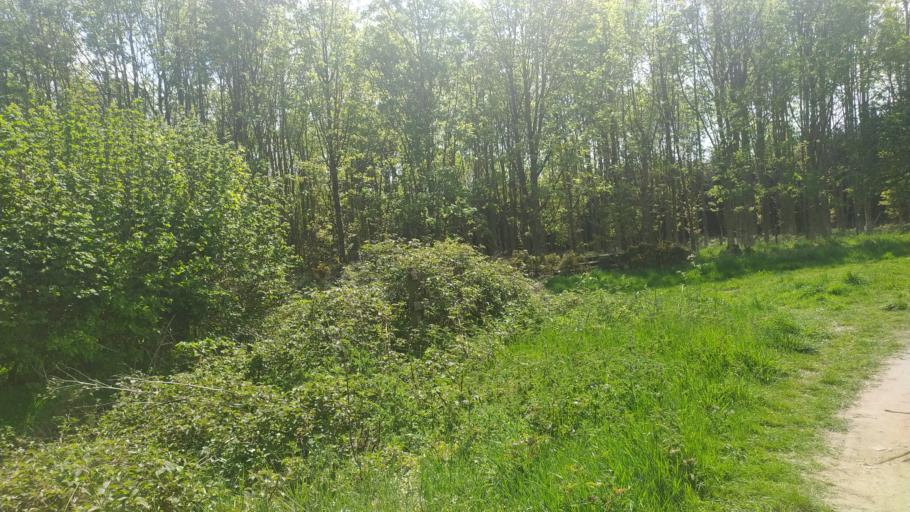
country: GB
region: England
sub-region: City and Borough of Leeds
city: Chapel Allerton
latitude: 53.8822
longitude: -1.5465
